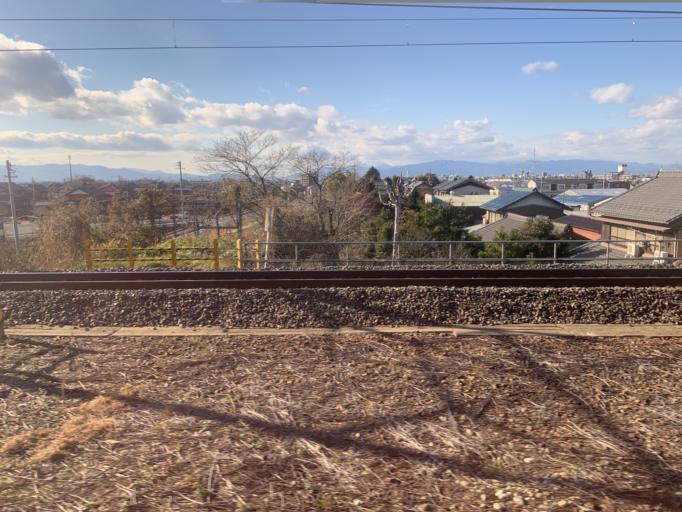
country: JP
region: Gifu
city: Kasamatsucho
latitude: 35.3755
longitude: 136.7811
